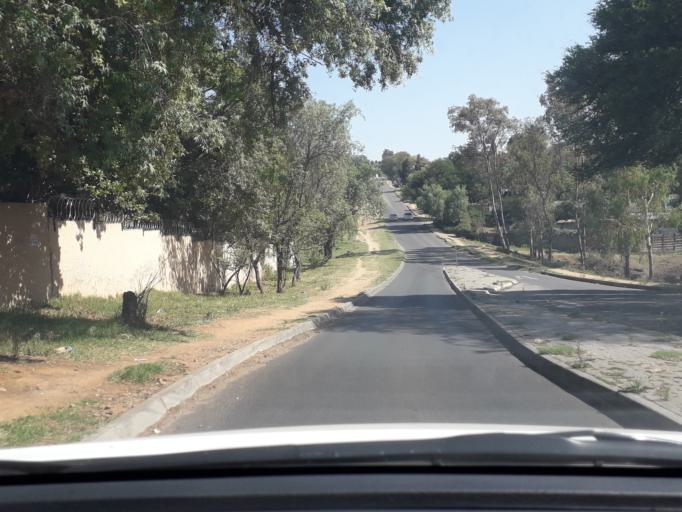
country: ZA
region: Gauteng
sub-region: City of Johannesburg Metropolitan Municipality
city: Roodepoort
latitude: -26.0850
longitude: 27.9464
